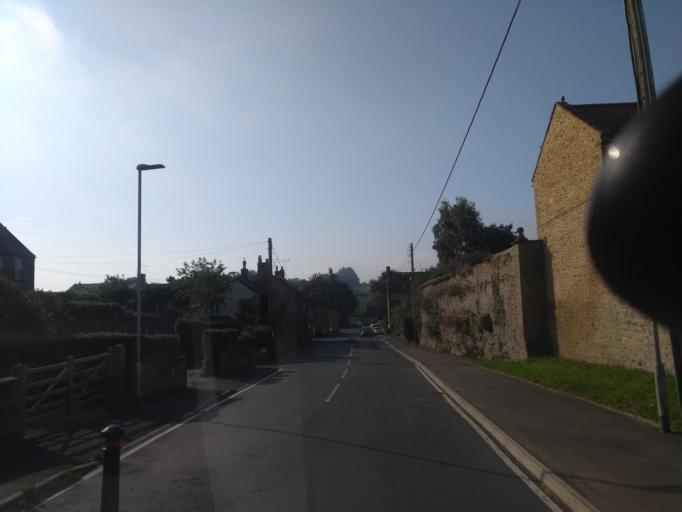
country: GB
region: England
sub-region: Somerset
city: Merriott
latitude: 50.9068
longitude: -2.7949
